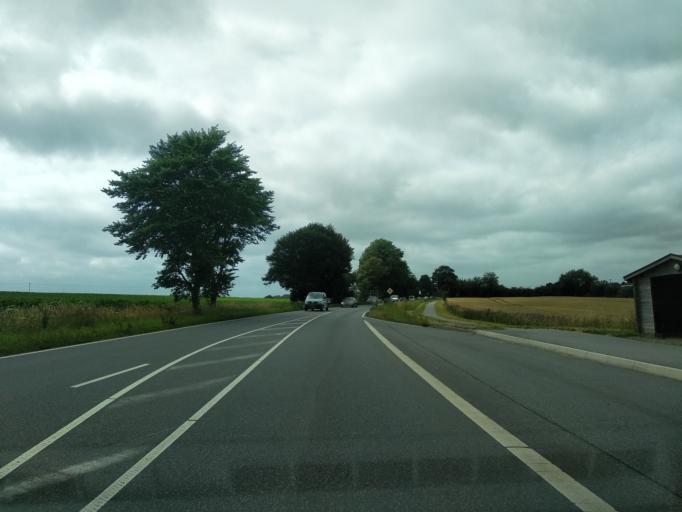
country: DE
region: Schleswig-Holstein
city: Ringsberg
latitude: 54.8035
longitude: 9.5972
